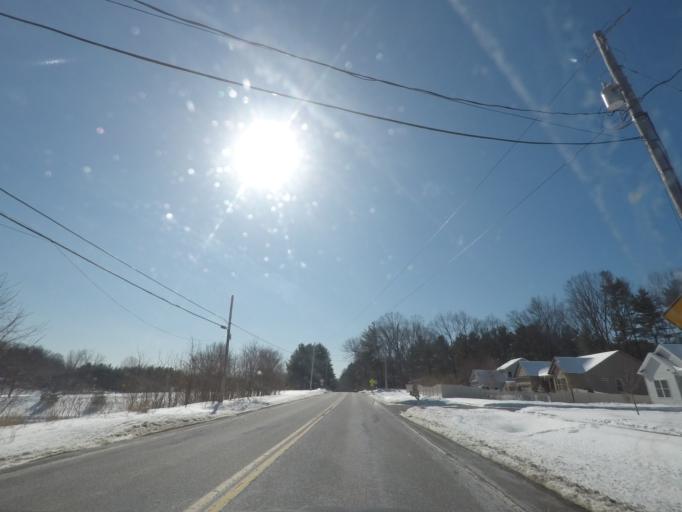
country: US
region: New York
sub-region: Saratoga County
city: Country Knolls
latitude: 42.9207
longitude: -73.8228
